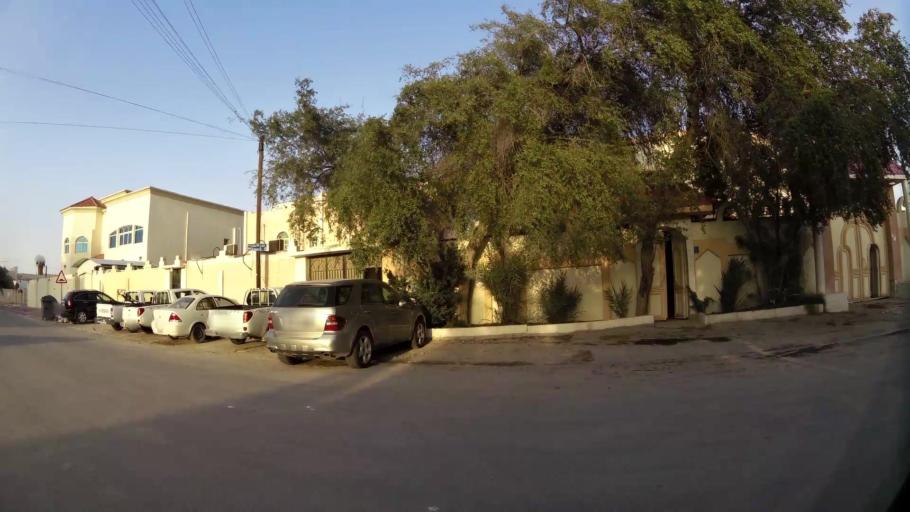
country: QA
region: Baladiyat ar Rayyan
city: Ar Rayyan
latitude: 25.3183
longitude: 51.4564
